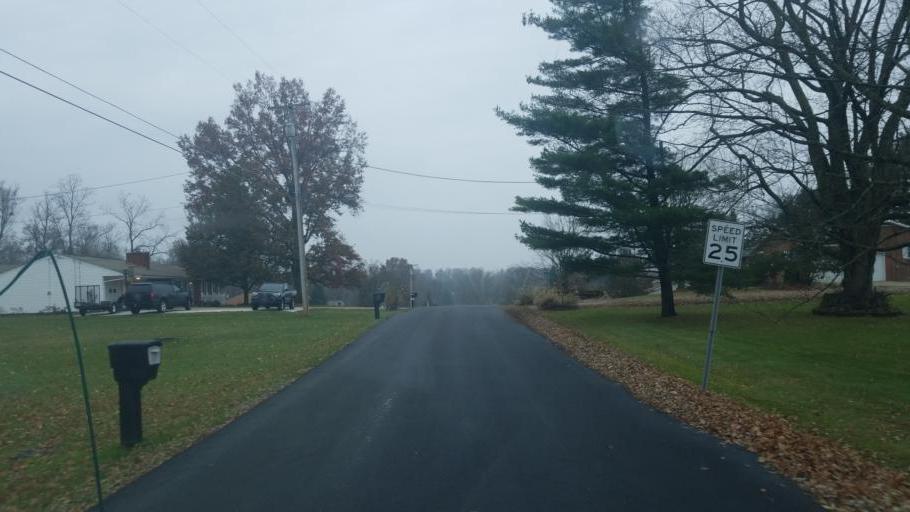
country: US
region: Ohio
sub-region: Richland County
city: Lexington
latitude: 40.6962
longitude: -82.5300
